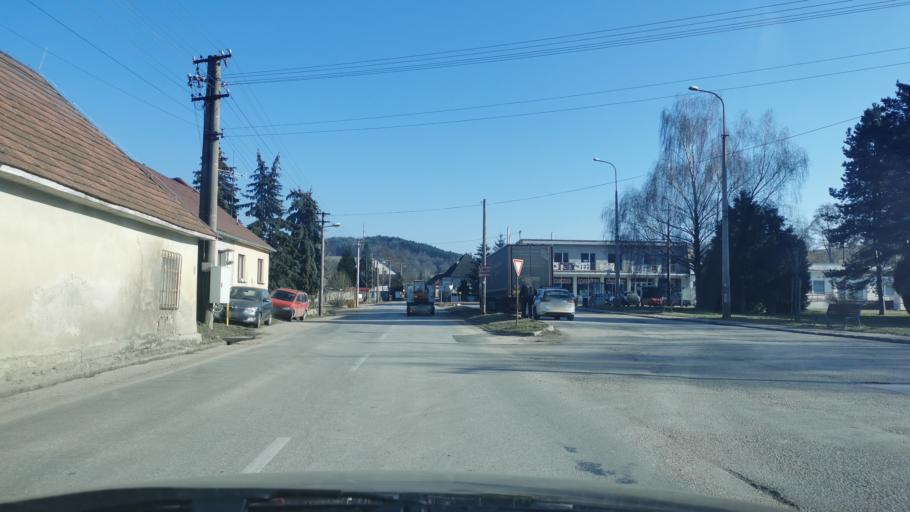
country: SK
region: Trenciansky
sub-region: Okres Myjava
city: Myjava
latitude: 48.7455
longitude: 17.5339
